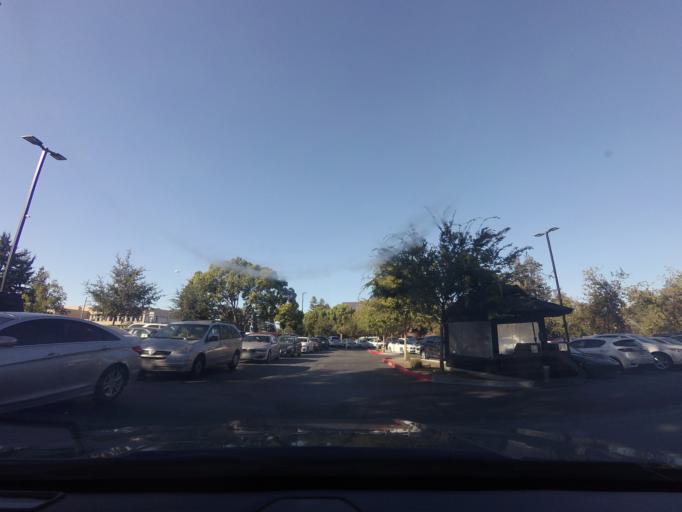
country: US
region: California
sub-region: Monterey County
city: Las Lomas
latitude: 36.8770
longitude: -121.7471
